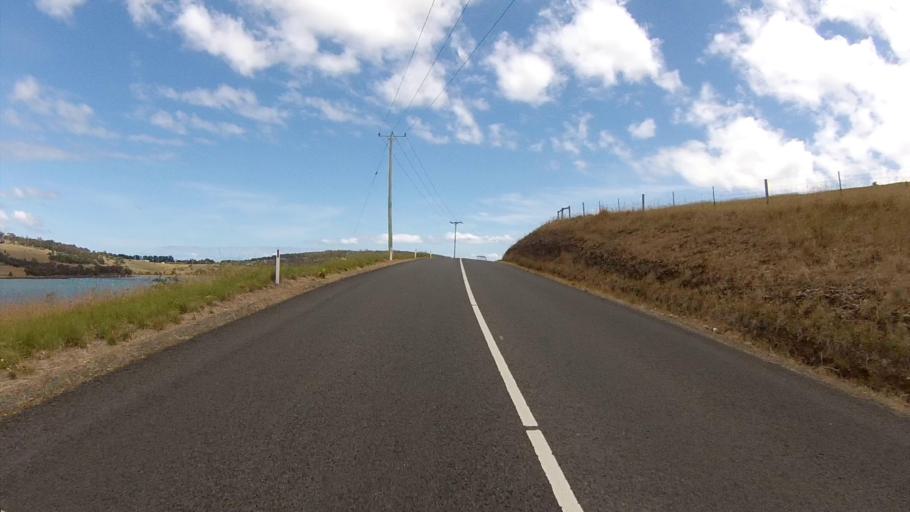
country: AU
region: Tasmania
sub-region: Sorell
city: Sorell
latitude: -42.8687
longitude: 147.6725
